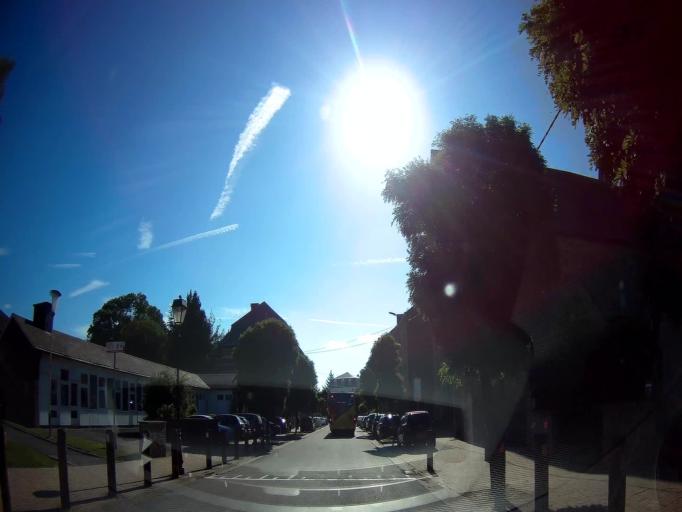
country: BE
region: Wallonia
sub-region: Province du Luxembourg
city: Bastogne
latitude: 49.9997
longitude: 5.7108
